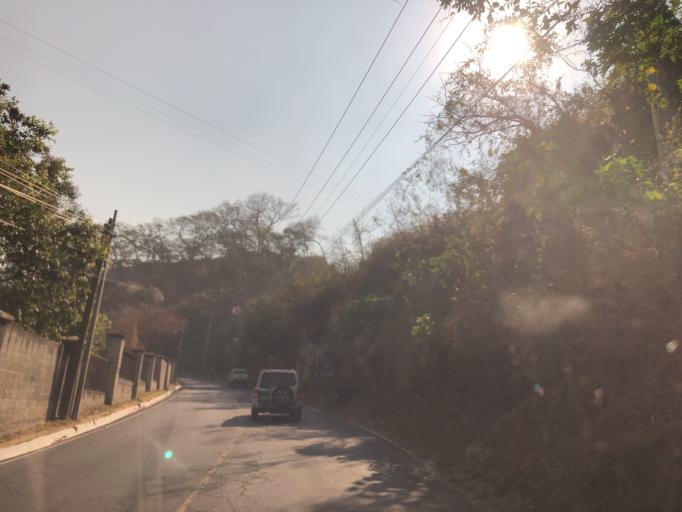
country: GT
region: Guatemala
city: Petapa
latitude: 14.5033
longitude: -90.5413
